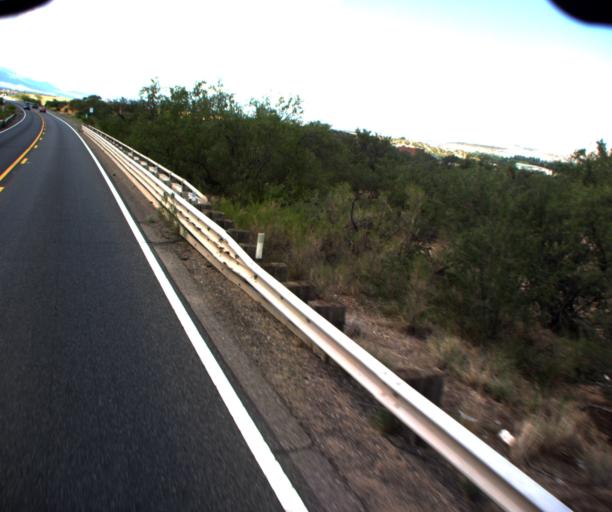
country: US
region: Arizona
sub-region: Yavapai County
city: Camp Verde
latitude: 34.6194
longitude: -111.9204
